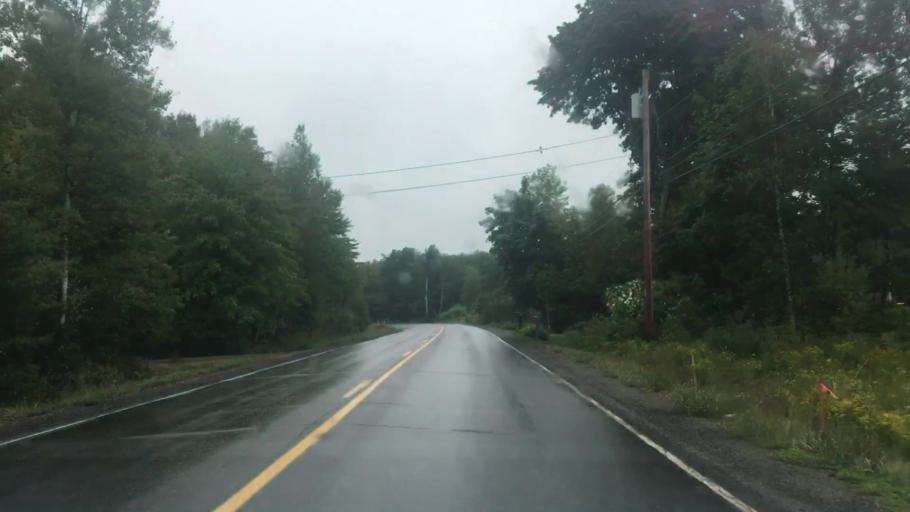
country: US
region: Maine
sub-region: Penobscot County
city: Milford
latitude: 44.9645
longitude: -68.7175
